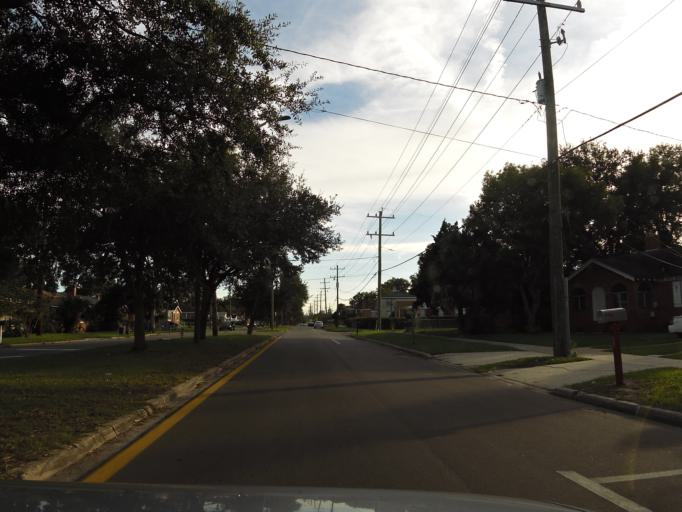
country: US
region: Florida
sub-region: Duval County
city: Jacksonville
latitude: 30.3770
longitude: -81.6568
